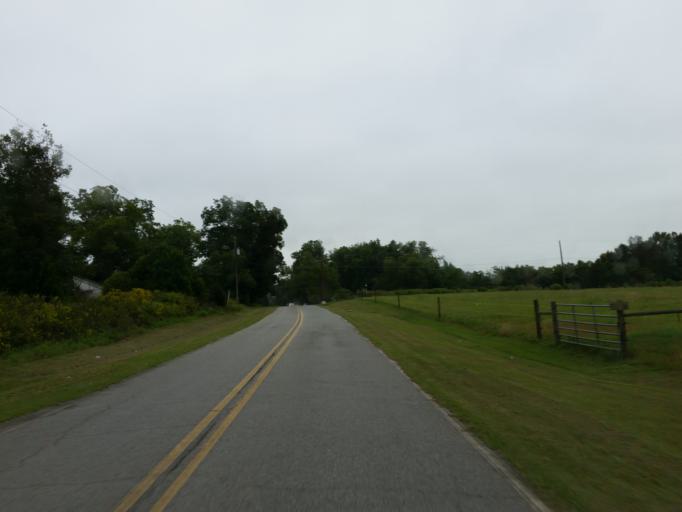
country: US
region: Georgia
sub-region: Dooly County
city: Unadilla
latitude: 32.2708
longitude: -83.7387
